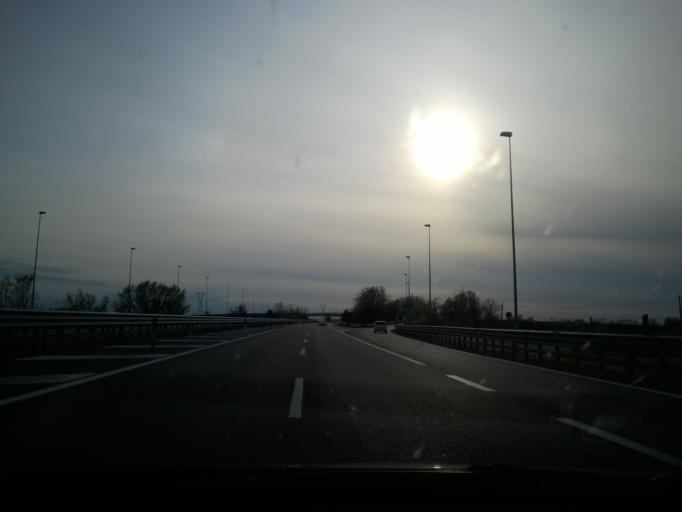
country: IT
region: Emilia-Romagna
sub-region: Provincia di Piacenza
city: Monticelli d'Ongina
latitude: 45.0620
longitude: 9.9448
